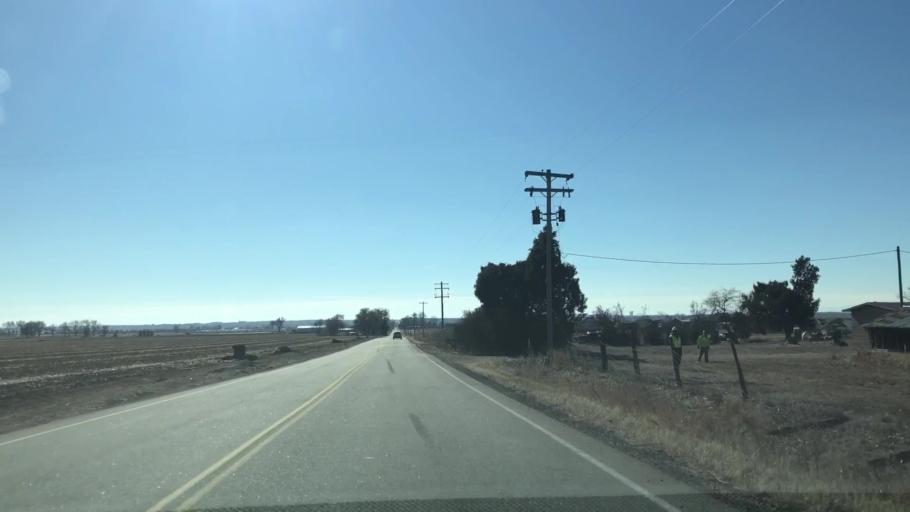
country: US
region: Colorado
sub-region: Weld County
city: Windsor
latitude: 40.5184
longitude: -104.9443
